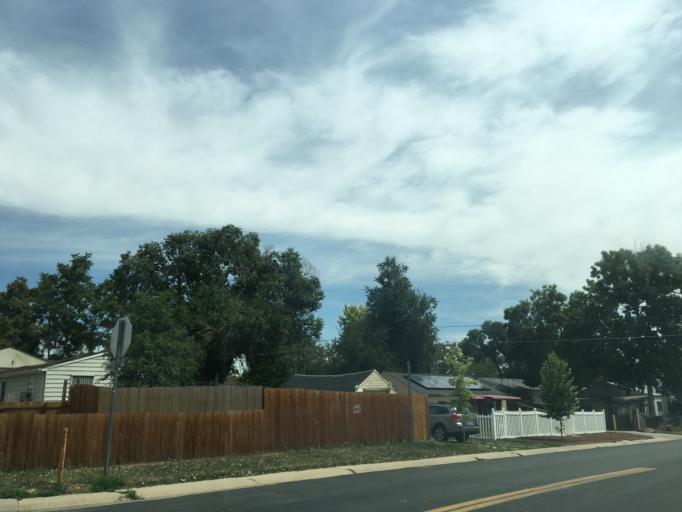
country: US
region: Colorado
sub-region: Jefferson County
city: Lakewood
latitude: 39.6967
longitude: -105.0390
